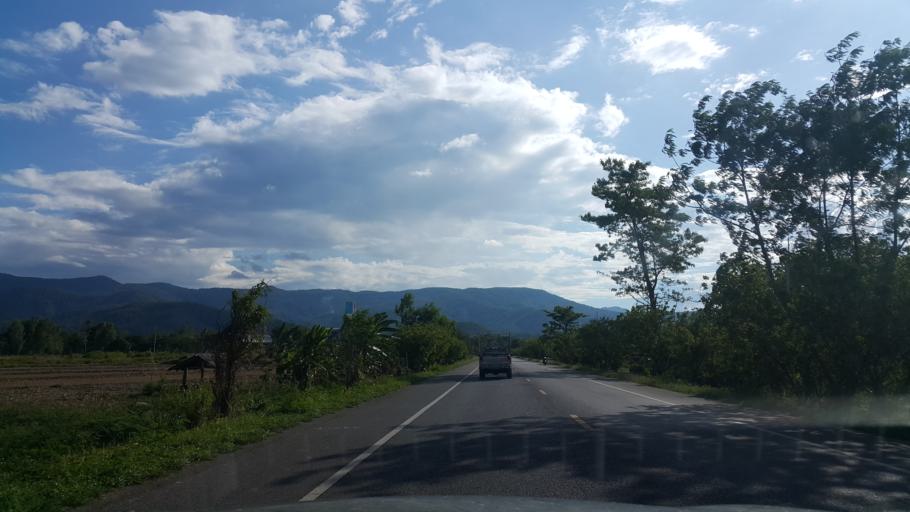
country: TH
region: Phayao
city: Phayao
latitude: 19.0816
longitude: 99.8745
